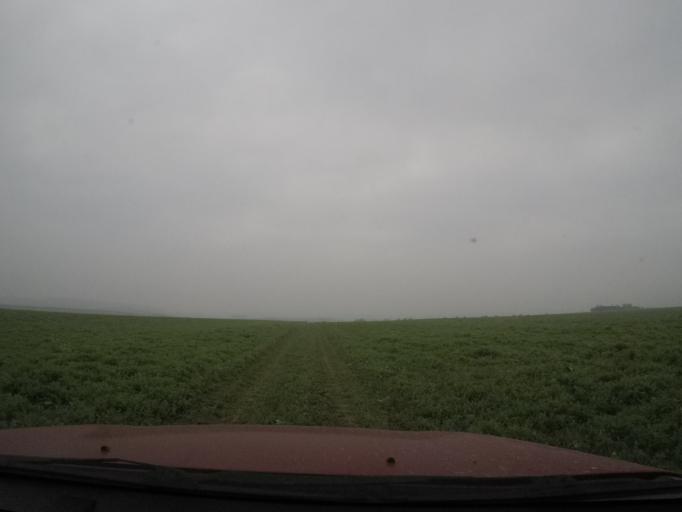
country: SK
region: Presovsky
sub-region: Okres Presov
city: Presov
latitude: 48.8872
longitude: 21.2704
